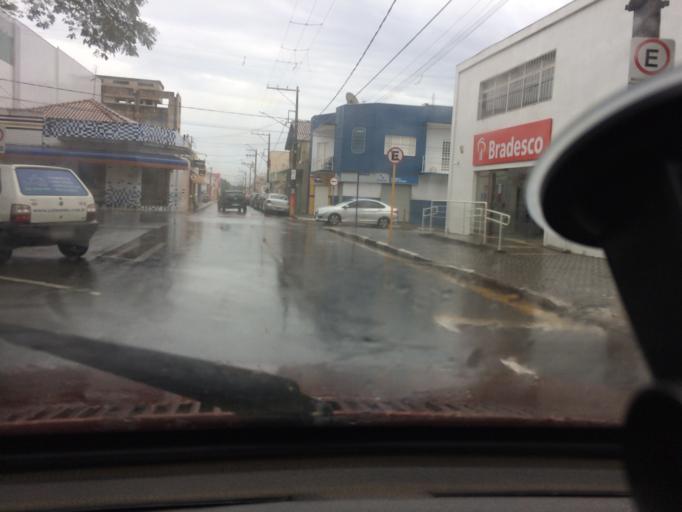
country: BR
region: Sao Paulo
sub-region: Capao Bonito
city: Capao Bonito
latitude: -24.0055
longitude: -48.3499
